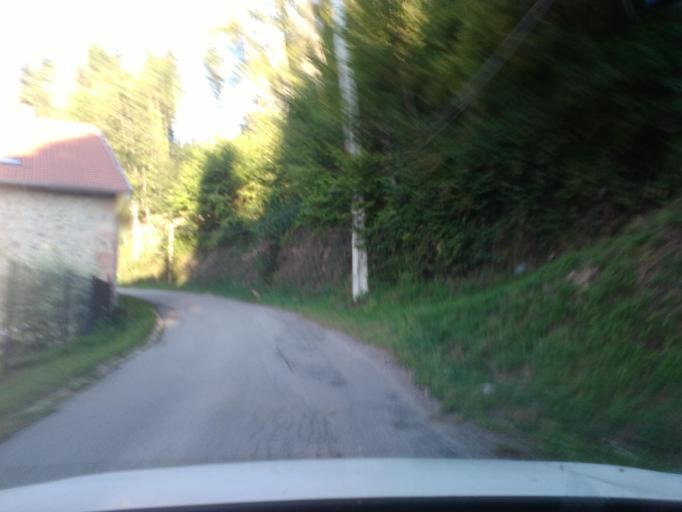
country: FR
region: Lorraine
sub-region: Departement des Vosges
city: Ban-de-Laveline
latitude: 48.3380
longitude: 7.0803
